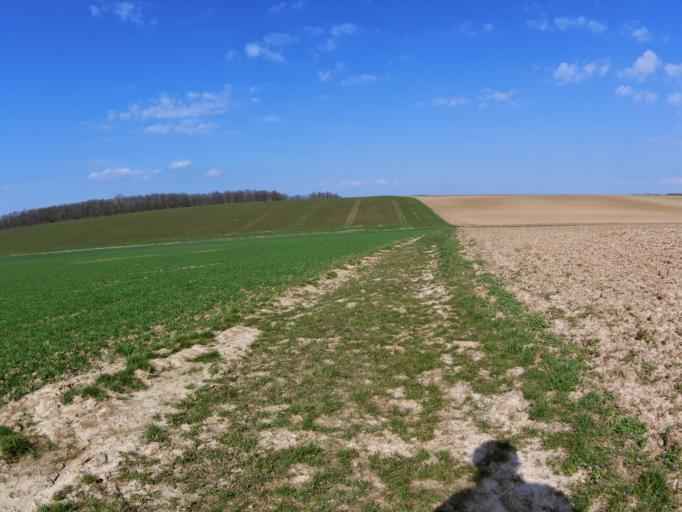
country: DE
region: Bavaria
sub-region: Regierungsbezirk Unterfranken
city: Rottendorf
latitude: 49.7985
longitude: 10.0603
